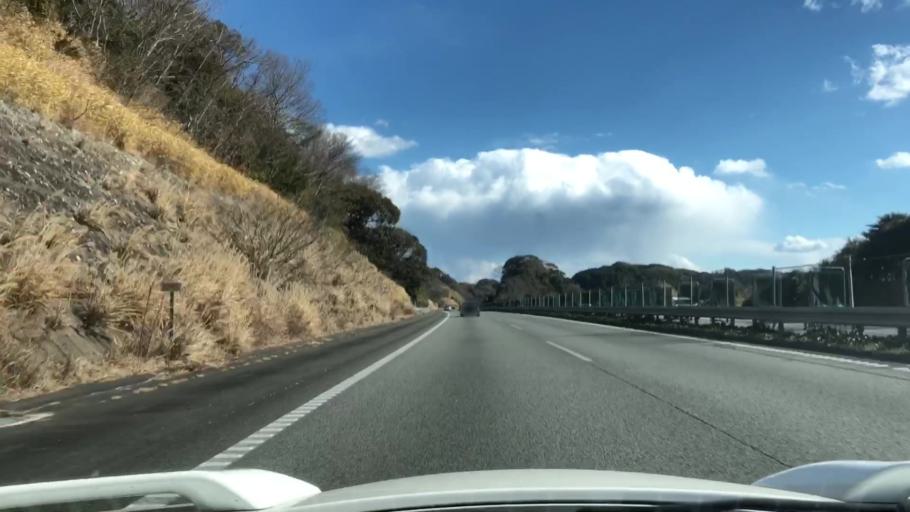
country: JP
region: Shizuoka
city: Kakegawa
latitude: 34.7616
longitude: 138.0414
